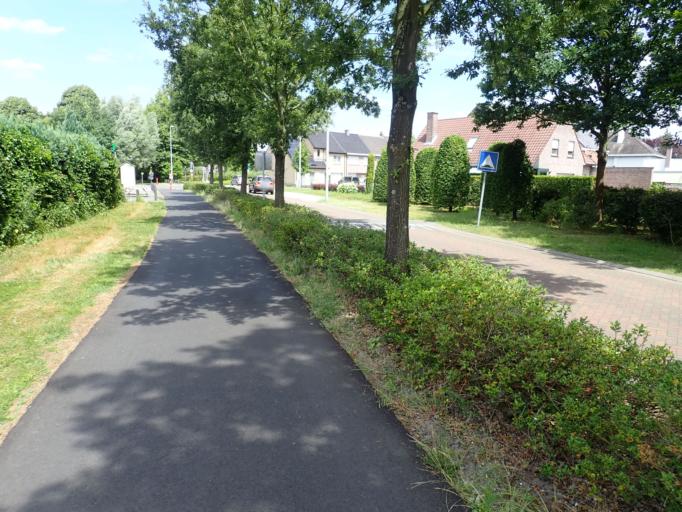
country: BE
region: Flanders
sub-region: Provincie Oost-Vlaanderen
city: Hamme
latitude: 51.0892
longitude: 4.1317
